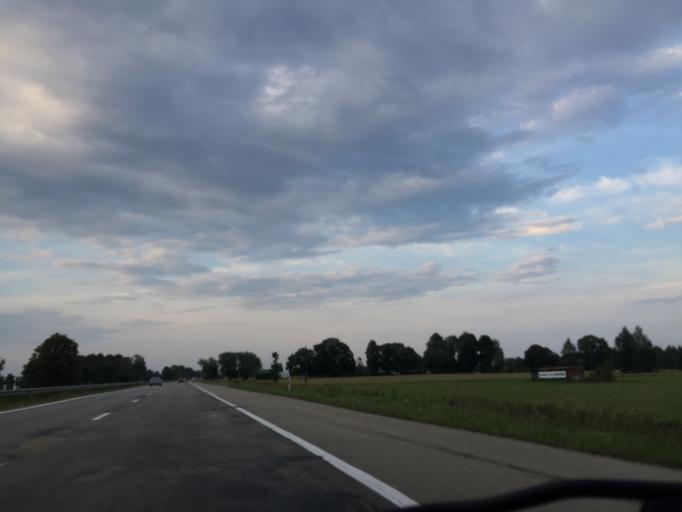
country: LV
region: Olaine
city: Olaine
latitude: 56.7711
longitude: 23.9262
